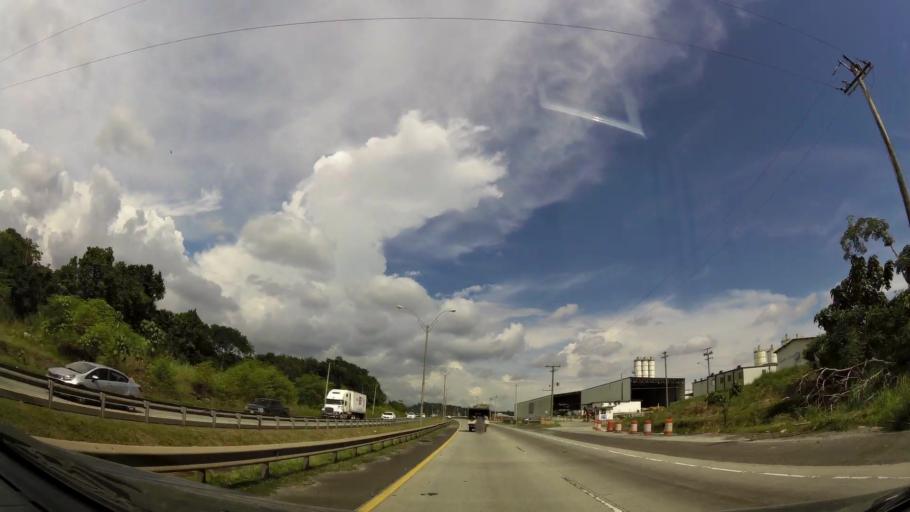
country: PA
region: Panama
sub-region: Distrito de Panama
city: Paraiso
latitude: 9.0289
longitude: -79.5877
